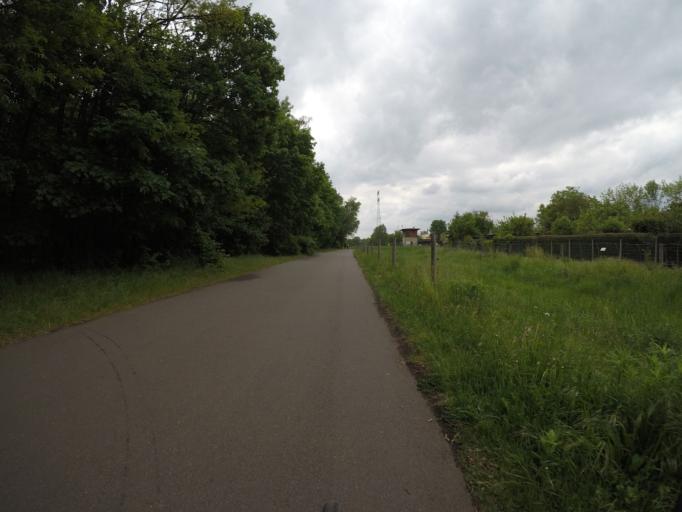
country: DE
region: Berlin
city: Lichtenberg
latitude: 52.5239
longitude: 13.5051
